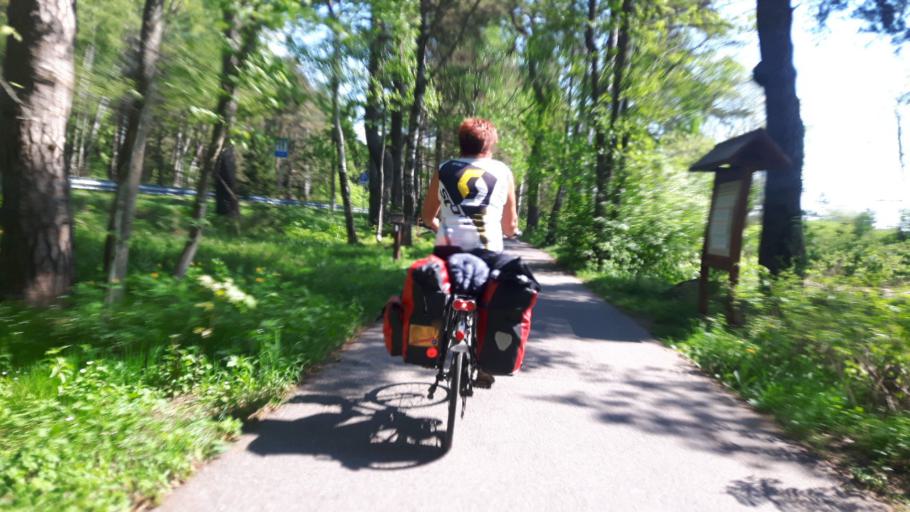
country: RU
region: St.-Petersburg
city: Komarovo
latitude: 60.1773
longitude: 29.7905
